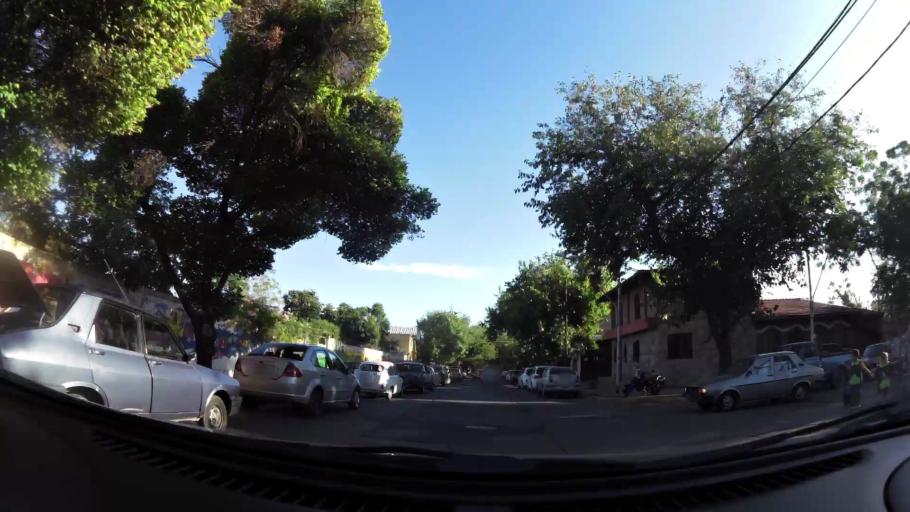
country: AR
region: Mendoza
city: Las Heras
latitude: -32.8677
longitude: -68.8273
